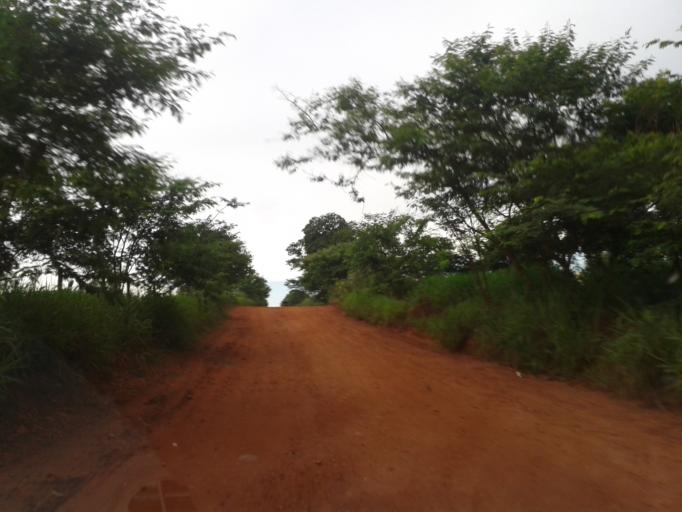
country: BR
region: Minas Gerais
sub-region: Santa Vitoria
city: Santa Vitoria
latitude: -19.1097
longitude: -50.5192
